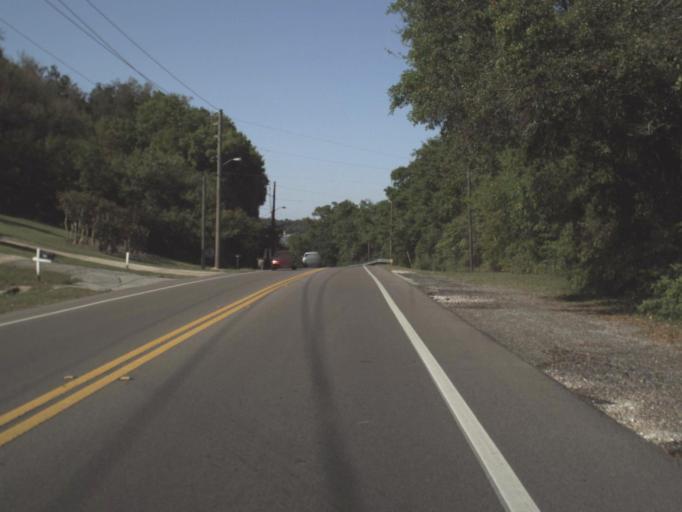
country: US
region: Florida
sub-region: Escambia County
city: East Pensacola Heights
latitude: 30.4671
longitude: -87.1616
